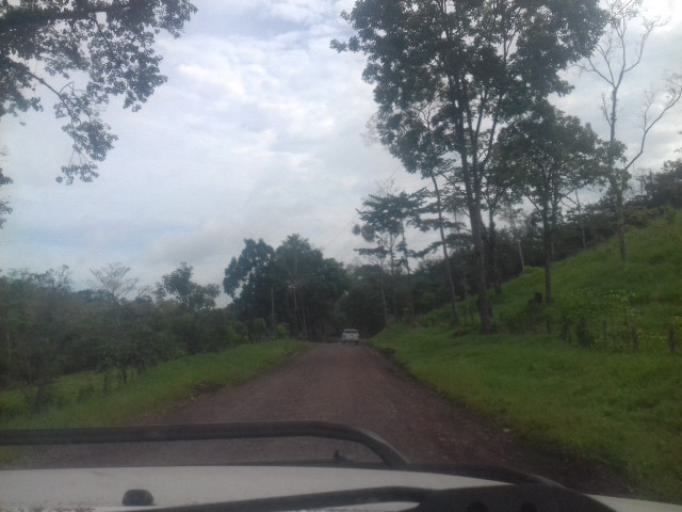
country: NI
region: Atlantico Norte (RAAN)
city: Waslala
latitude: 13.4221
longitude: -85.3158
